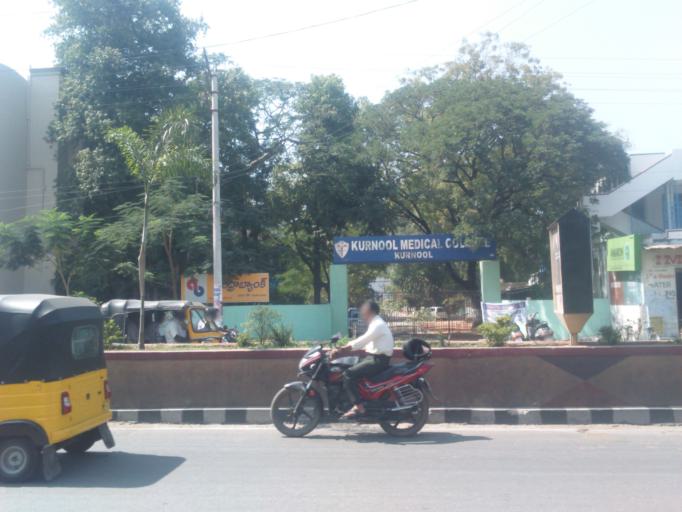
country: IN
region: Telangana
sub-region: Mahbubnagar
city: Alampur
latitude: 15.8219
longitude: 78.0404
